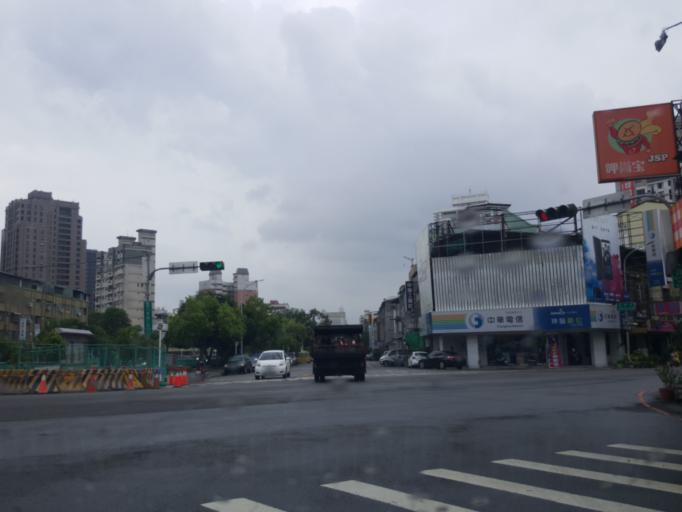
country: TW
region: Taiwan
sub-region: Taichung City
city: Taichung
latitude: 24.1320
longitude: 120.6632
